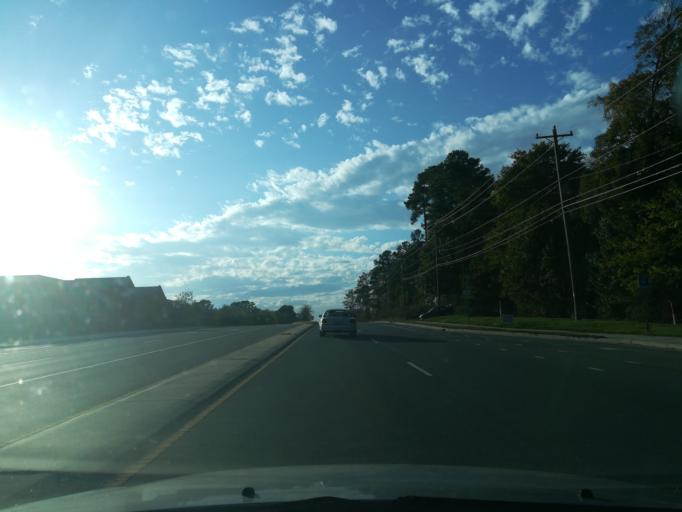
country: US
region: North Carolina
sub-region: Orange County
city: Chapel Hill
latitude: 35.9640
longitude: -79.0522
